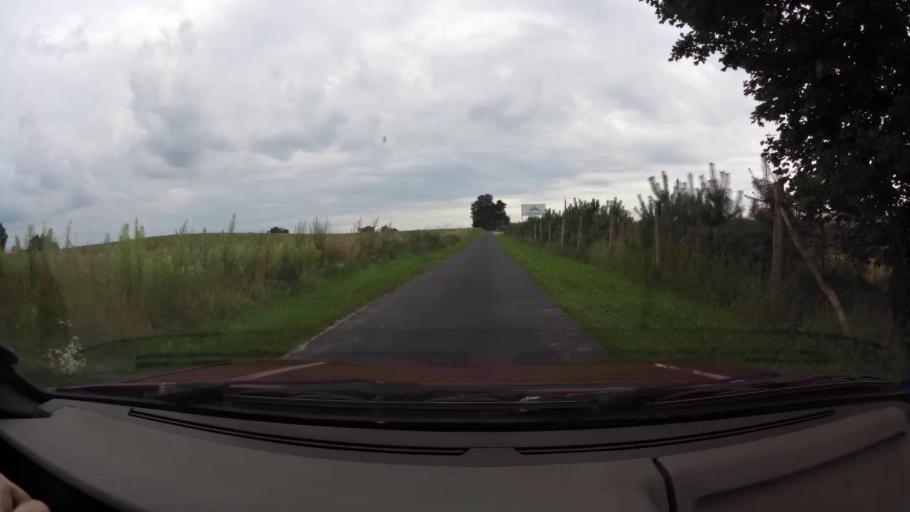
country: PL
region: West Pomeranian Voivodeship
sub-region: Powiat drawski
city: Drawsko Pomorskie
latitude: 53.5195
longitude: 15.7524
